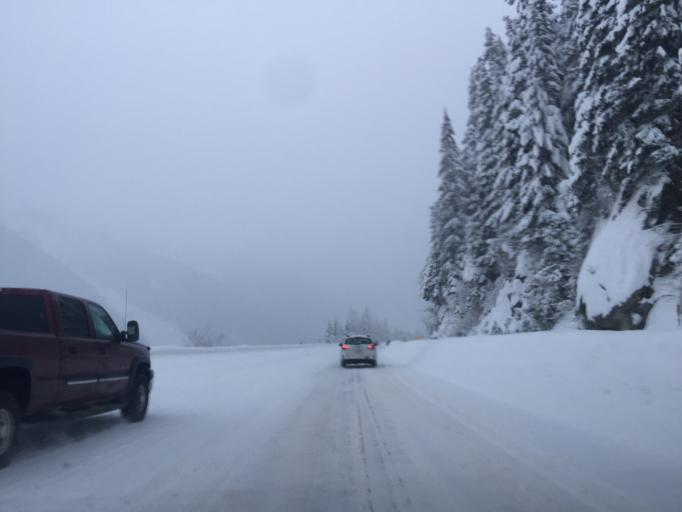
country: US
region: Washington
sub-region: Chelan County
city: Leavenworth
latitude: 47.7244
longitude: -121.1378
